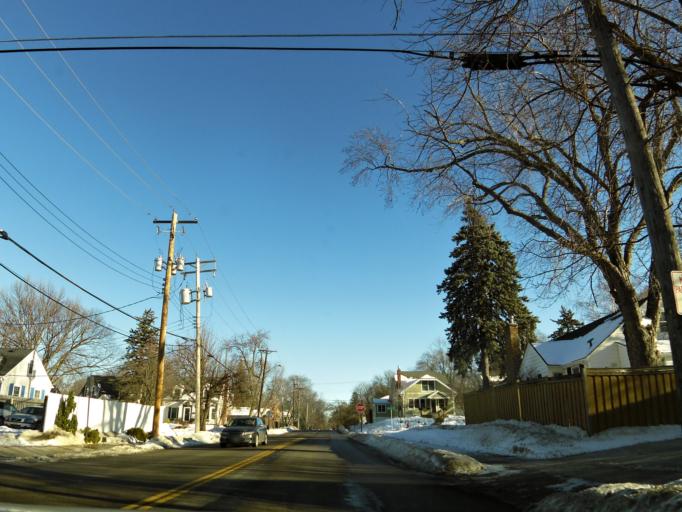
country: US
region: Minnesota
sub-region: Hennepin County
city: Saint Louis Park
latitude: 44.9342
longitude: -93.3362
